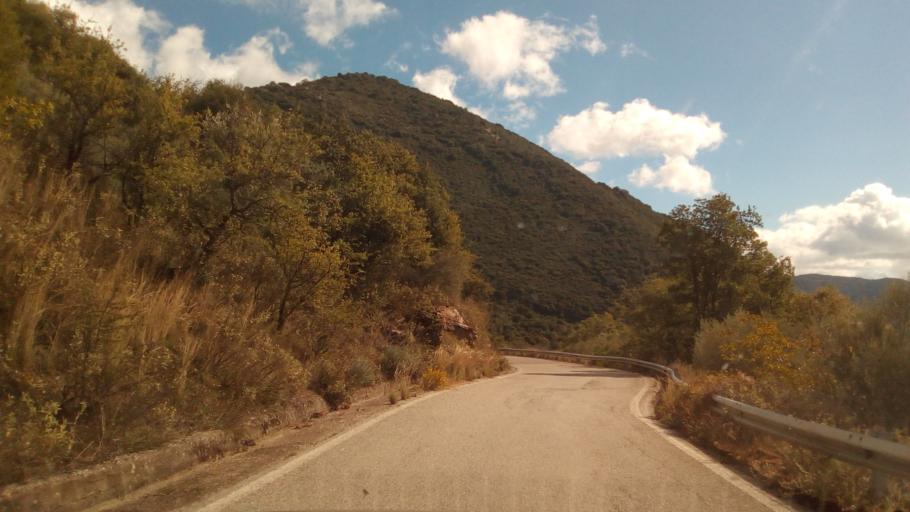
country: GR
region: West Greece
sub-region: Nomos Aitolias kai Akarnanias
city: Nafpaktos
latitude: 38.4799
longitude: 21.8643
